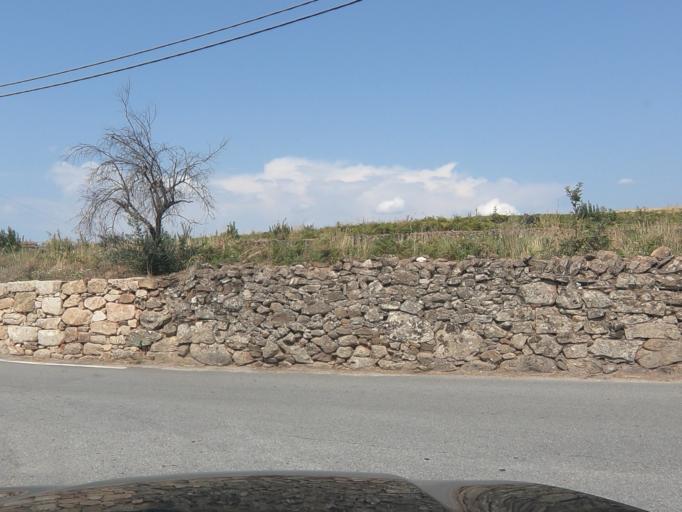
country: PT
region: Vila Real
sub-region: Sabrosa
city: Sabrosa
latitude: 41.3364
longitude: -7.5929
